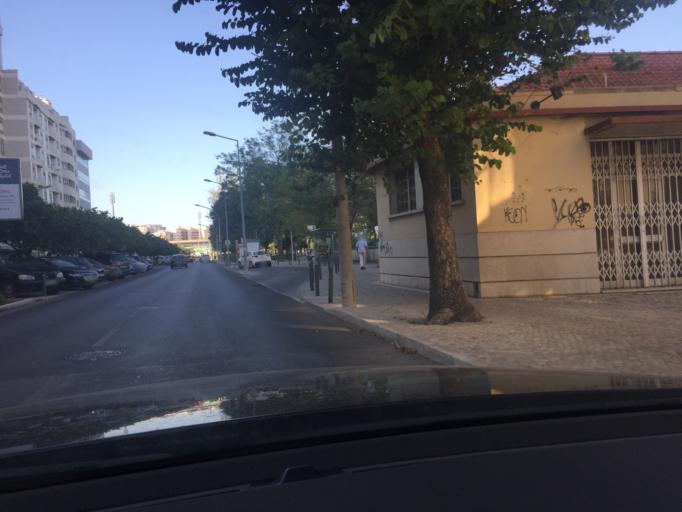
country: PT
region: Setubal
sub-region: Setubal
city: Setubal
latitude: 38.5272
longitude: -8.8931
